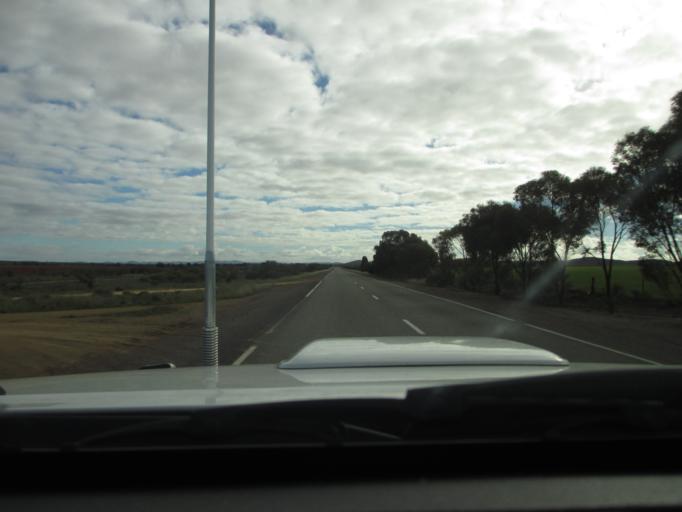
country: AU
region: South Australia
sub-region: Flinders Ranges
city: Quorn
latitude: -32.4463
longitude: 138.5362
